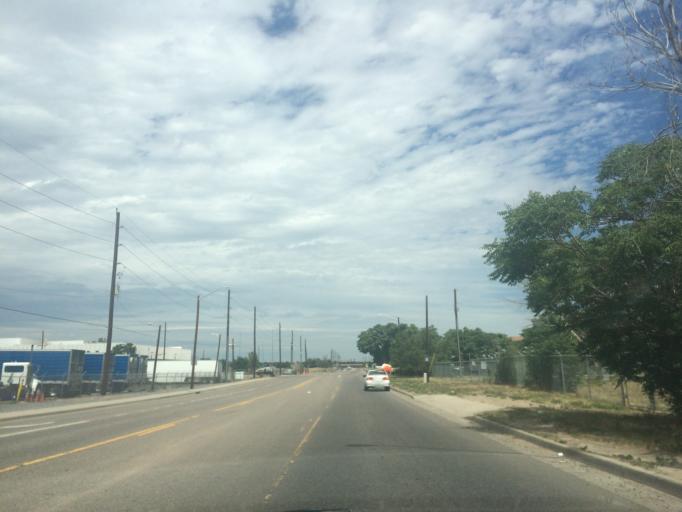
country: US
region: Colorado
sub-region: Adams County
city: Welby
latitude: 39.8168
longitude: -104.9592
